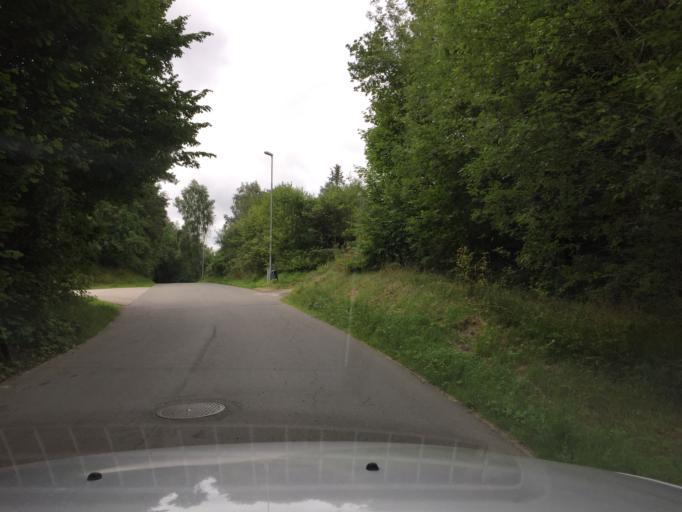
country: SE
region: Skane
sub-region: Hassleholms Kommun
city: Sosdala
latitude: 56.0331
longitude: 13.6718
